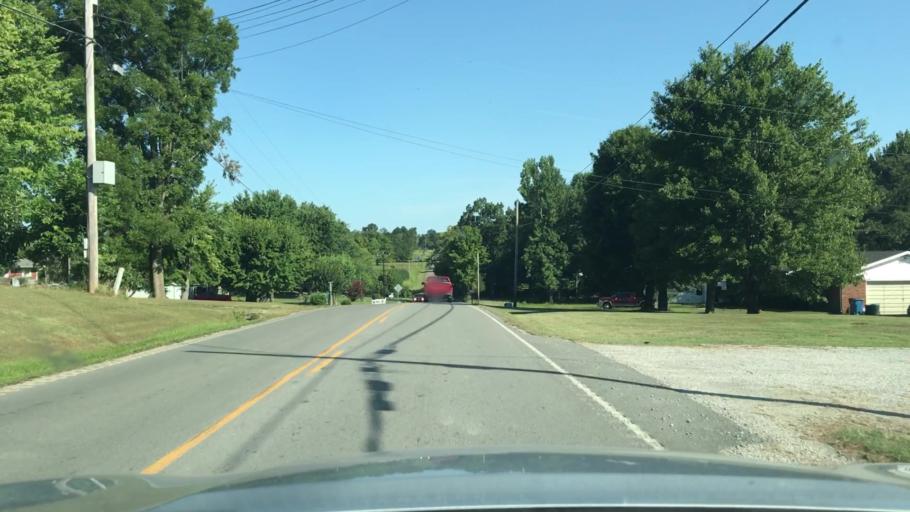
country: US
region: Kentucky
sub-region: Muhlenberg County
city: Greenville
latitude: 37.1667
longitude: -87.1469
